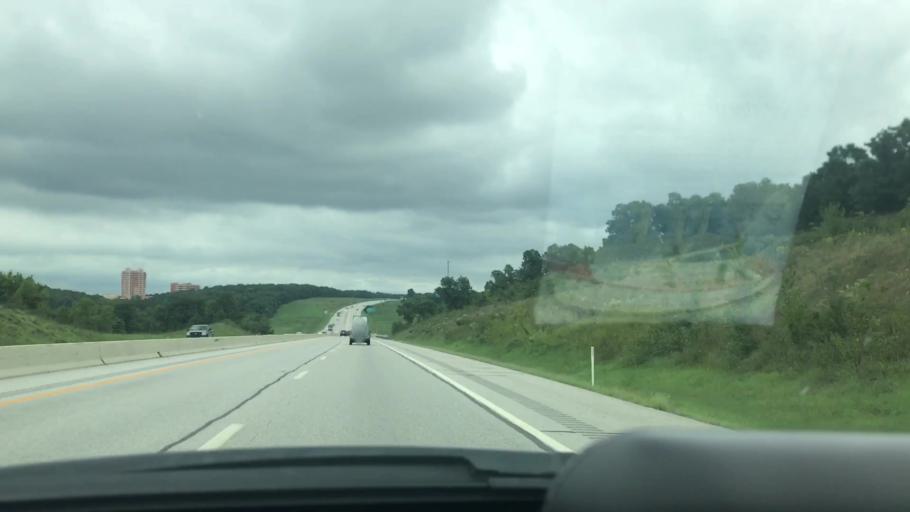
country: US
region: Kansas
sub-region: Cherokee County
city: Galena
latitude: 36.9825
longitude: -94.6350
